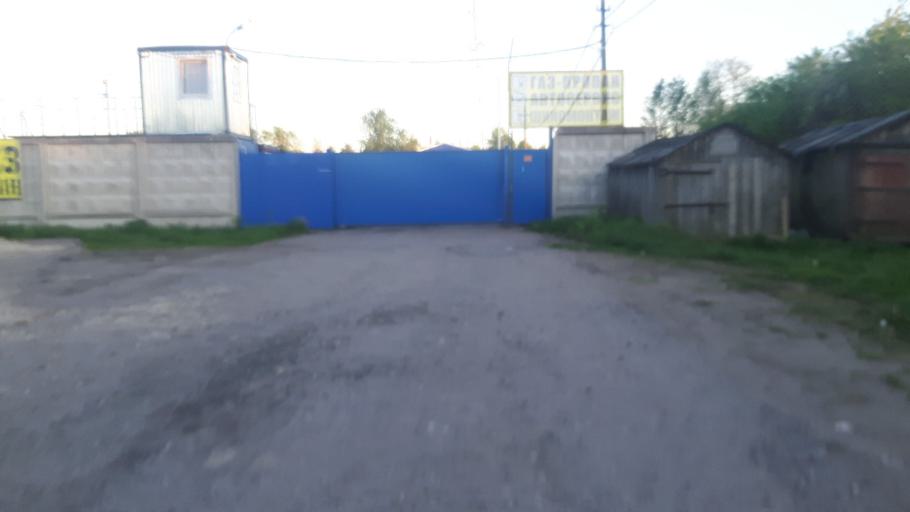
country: RU
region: St.-Petersburg
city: Bol'shaya Izhora
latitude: 59.9424
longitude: 29.5736
